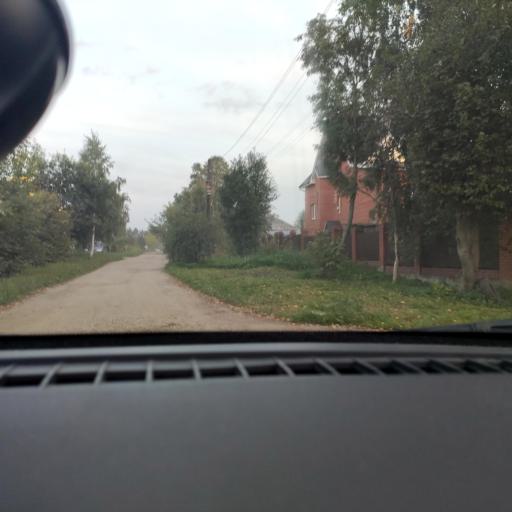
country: RU
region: Perm
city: Perm
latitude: 58.0400
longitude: 56.3453
